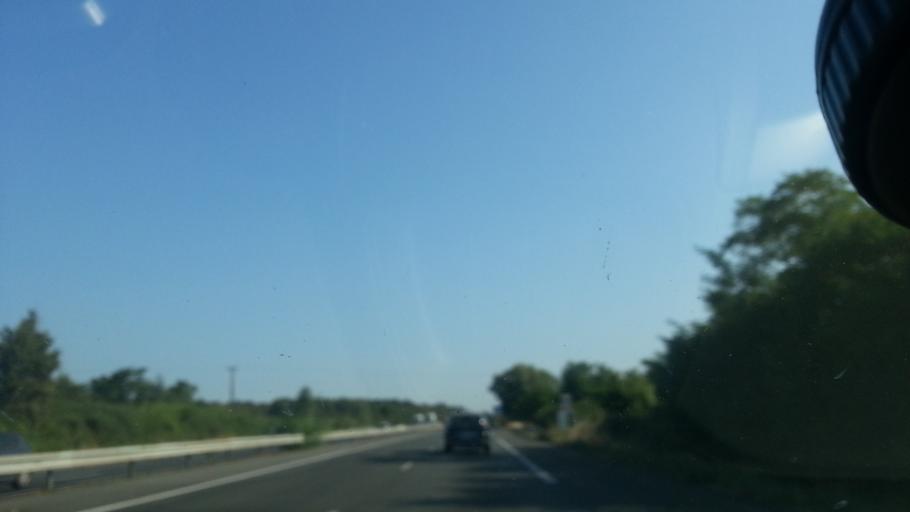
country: FR
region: Poitou-Charentes
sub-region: Departement de la Vienne
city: Antran
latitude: 46.8974
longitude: 0.5203
